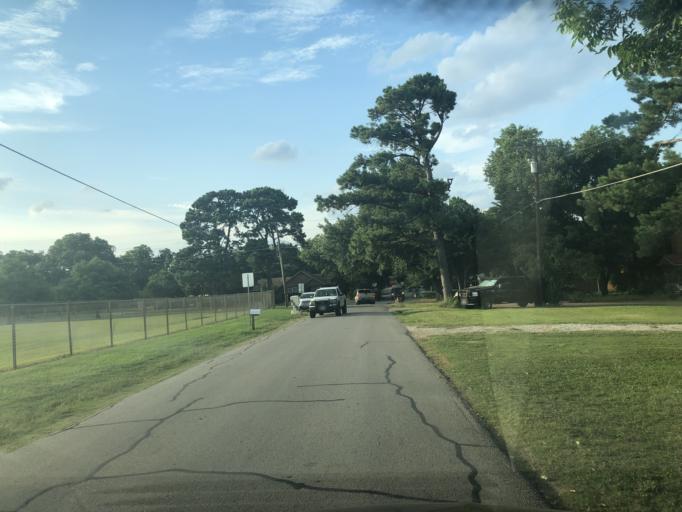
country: US
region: Texas
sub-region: Dallas County
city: Irving
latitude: 32.7932
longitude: -96.9431
